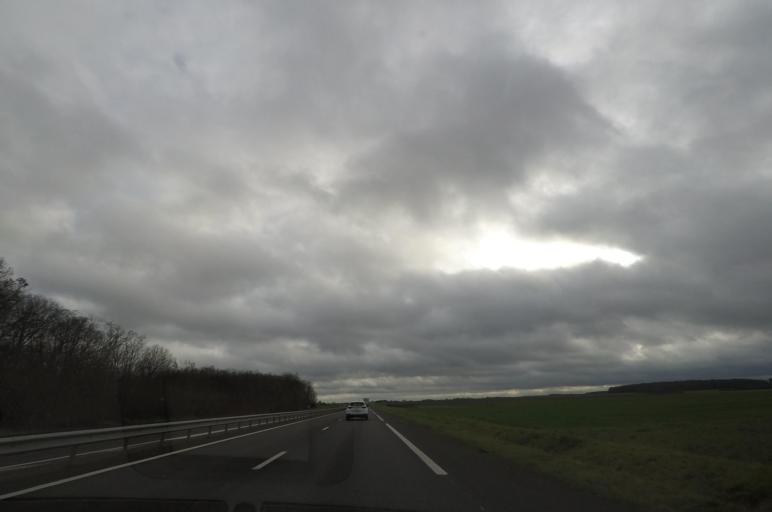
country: FR
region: Centre
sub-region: Departement du Loir-et-Cher
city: Saint-Sulpice-de-Pommeray
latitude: 47.6806
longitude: 1.2145
